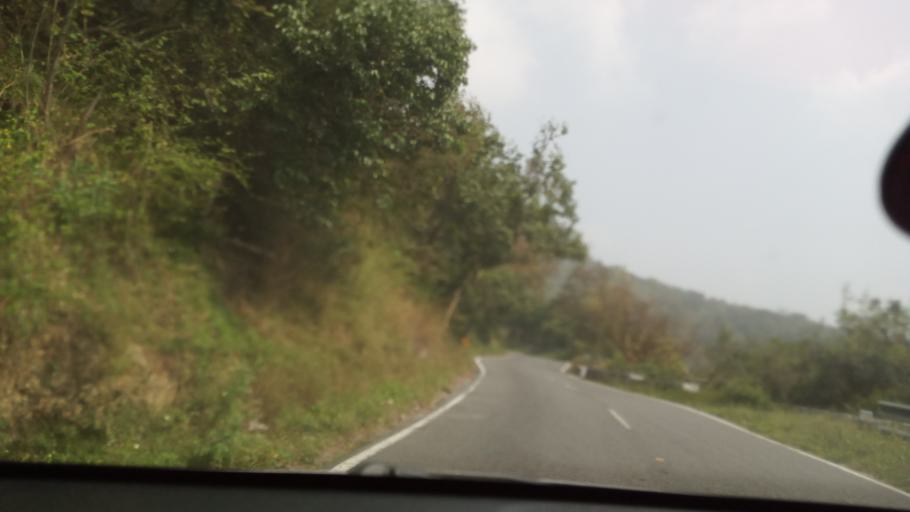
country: IN
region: Tamil Nadu
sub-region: Erode
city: Sathyamangalam
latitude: 11.5995
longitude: 77.1253
